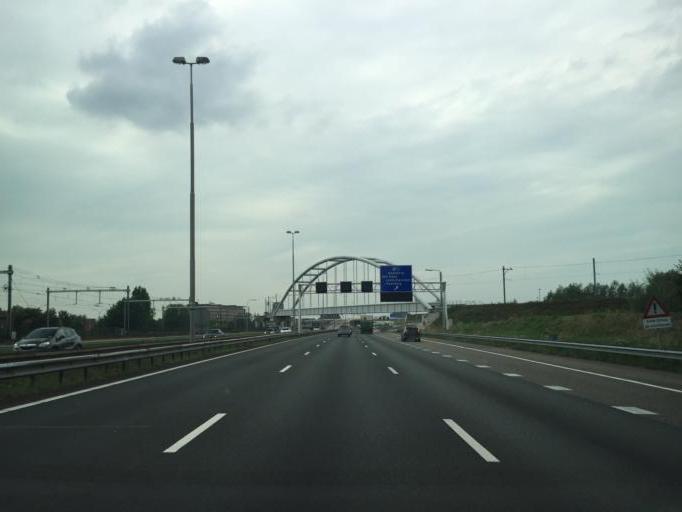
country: NL
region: South Holland
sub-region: Gemeente Pijnacker-Nootdorp
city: Pijnacker
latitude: 52.0529
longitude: 4.4102
